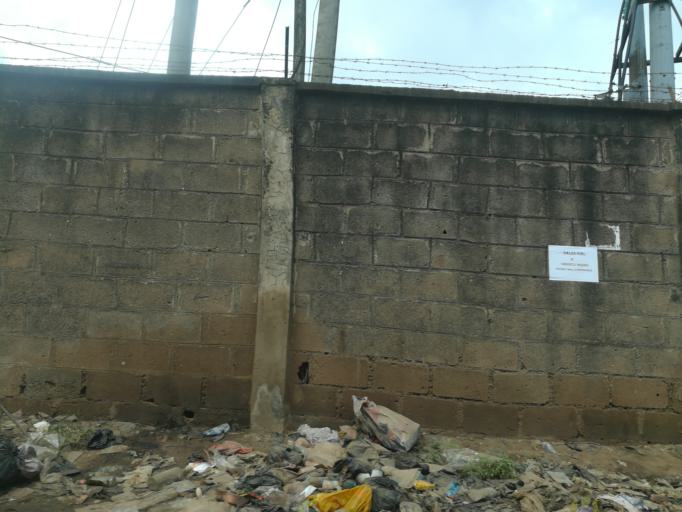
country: NG
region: Lagos
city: Ikorodu
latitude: 6.6250
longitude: 3.5066
